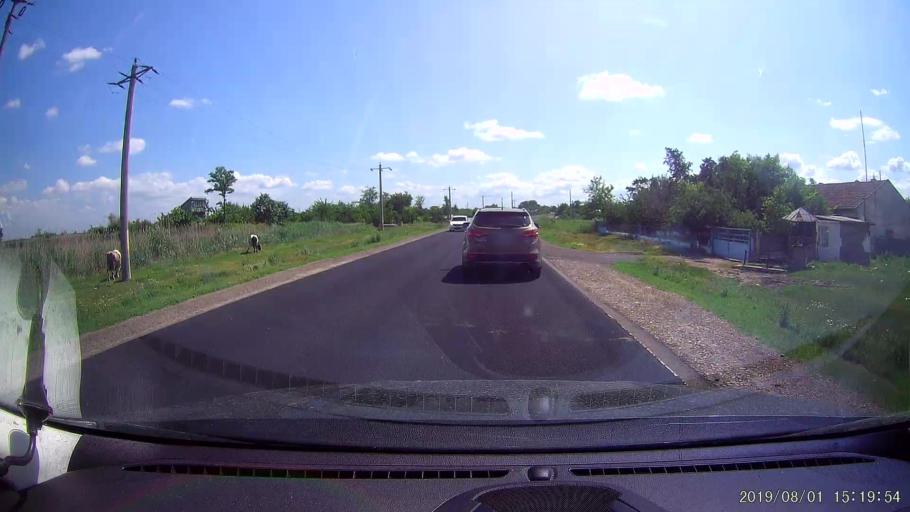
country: RO
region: Braila
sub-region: Comuna Unirea
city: Unirea
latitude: 45.0842
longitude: 27.8101
